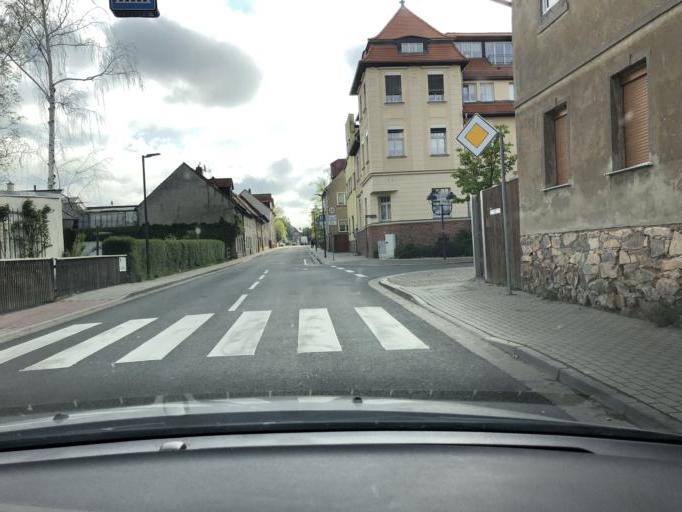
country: DE
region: Saxony
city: Rotha
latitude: 51.1984
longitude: 12.4135
